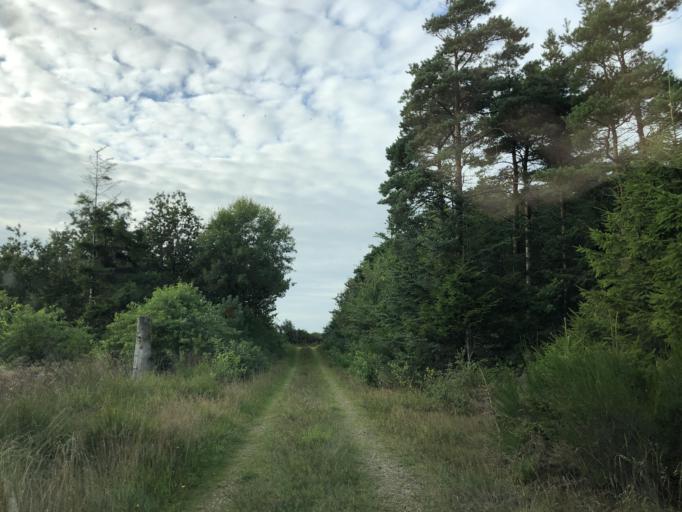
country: DK
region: Central Jutland
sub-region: Holstebro Kommune
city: Ulfborg
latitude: 56.2863
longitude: 8.4164
